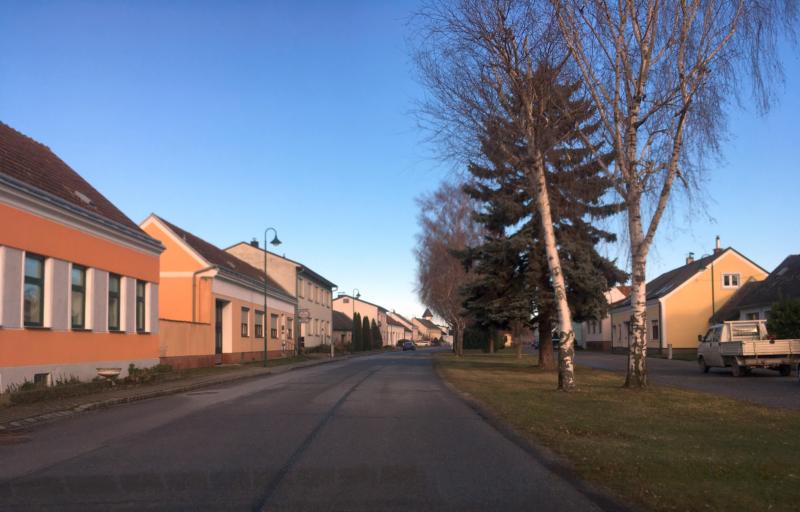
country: AT
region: Lower Austria
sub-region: Politischer Bezirk Bruck an der Leitha
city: Petronell-Carnuntum
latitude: 48.1487
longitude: 16.8347
